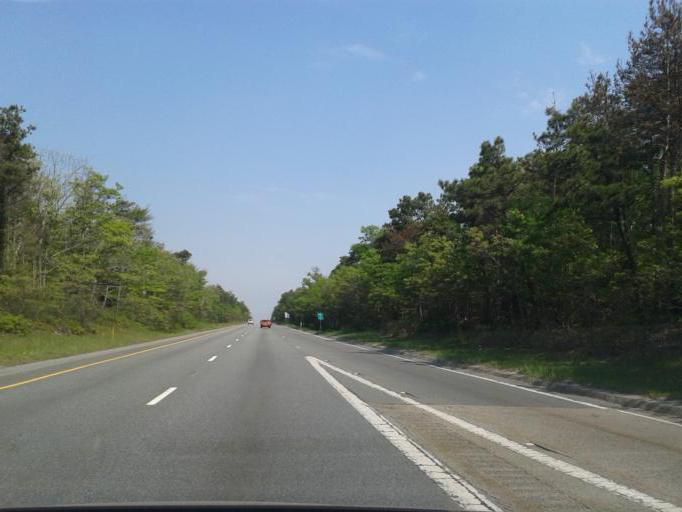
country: US
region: Massachusetts
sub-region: Barnstable County
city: Sagamore
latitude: 41.8176
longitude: -70.5554
